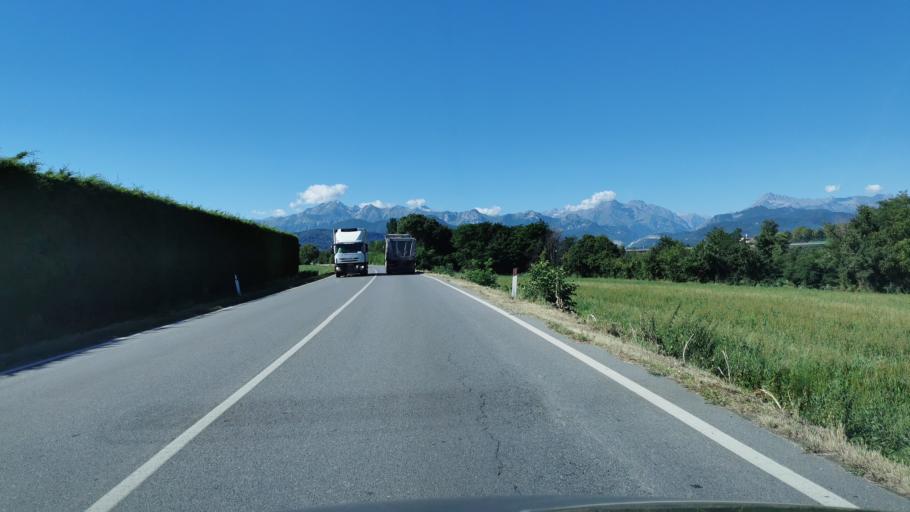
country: IT
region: Piedmont
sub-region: Provincia di Cuneo
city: Cuneo
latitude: 44.3771
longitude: 7.5549
